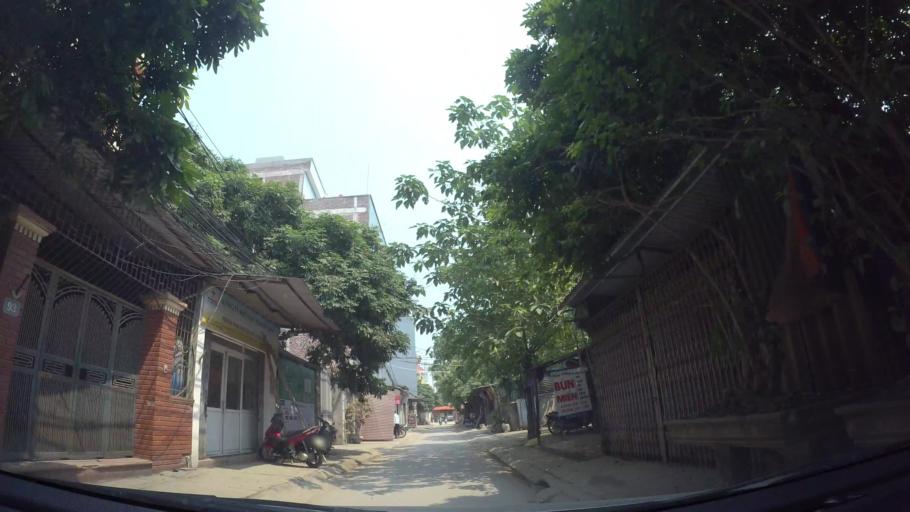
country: VN
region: Ha Noi
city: Ha Dong
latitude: 20.9894
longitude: 105.7717
